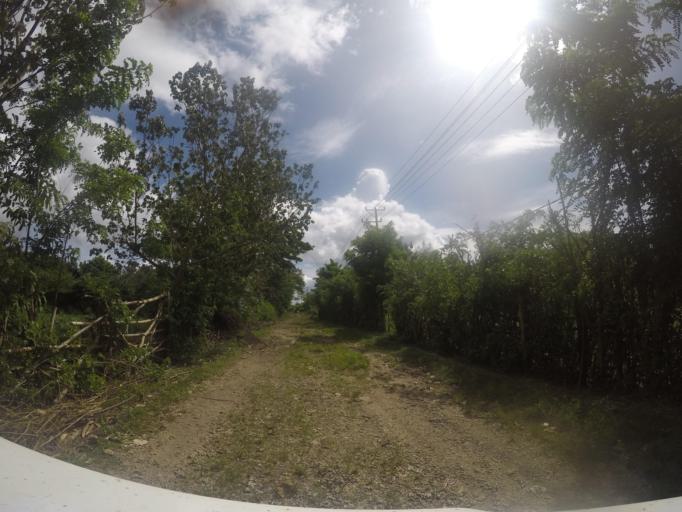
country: TL
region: Lautem
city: Lospalos
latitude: -8.4973
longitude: 127.0092
